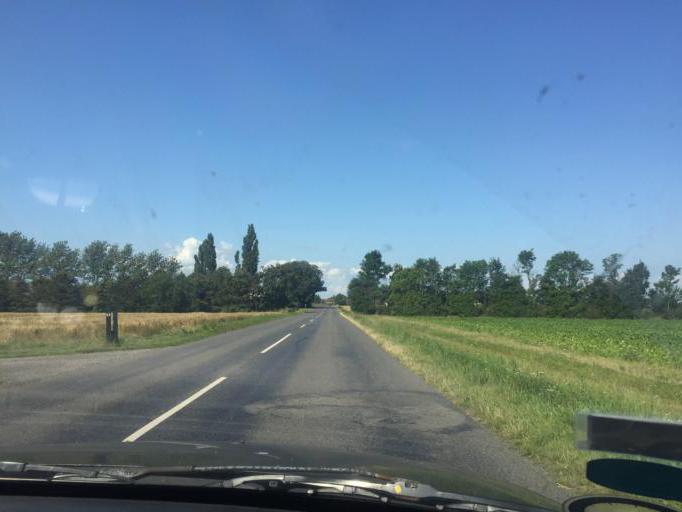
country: DK
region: Zealand
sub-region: Lolland Kommune
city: Maribo
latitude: 54.7960
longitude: 11.5356
